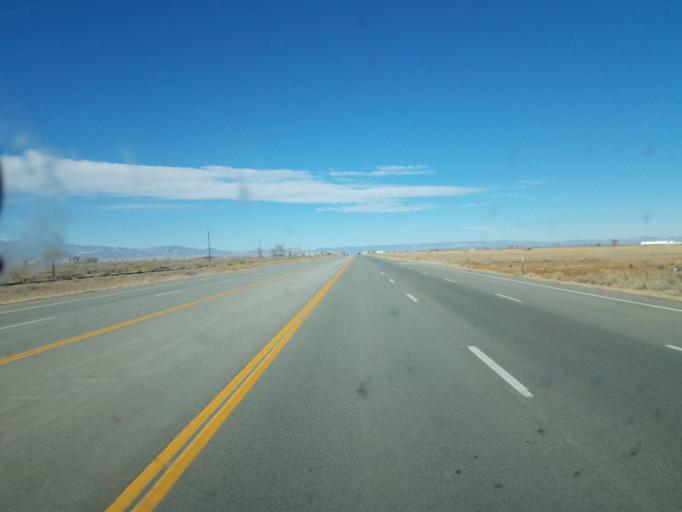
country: US
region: Colorado
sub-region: Alamosa County
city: Alamosa
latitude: 37.5222
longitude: -106.0055
